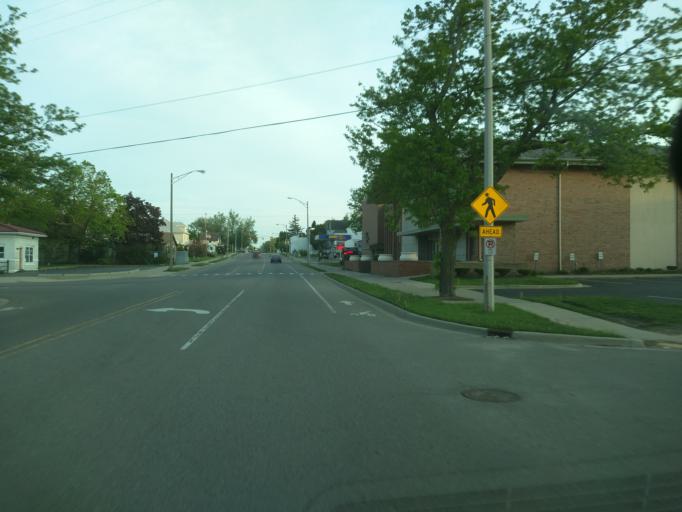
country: US
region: Michigan
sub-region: Ingham County
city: Lansing
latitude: 42.7169
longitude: -84.5524
